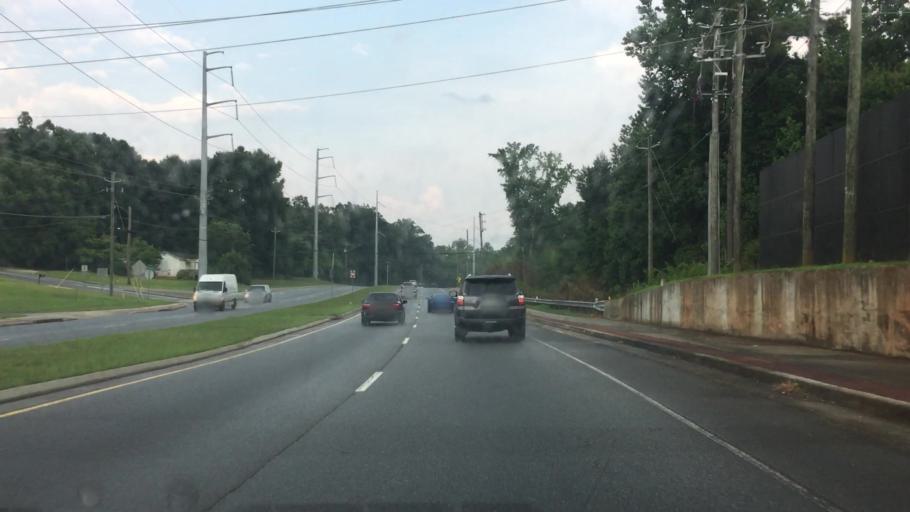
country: US
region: Georgia
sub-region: DeKalb County
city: Panthersville
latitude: 33.7041
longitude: -84.2140
